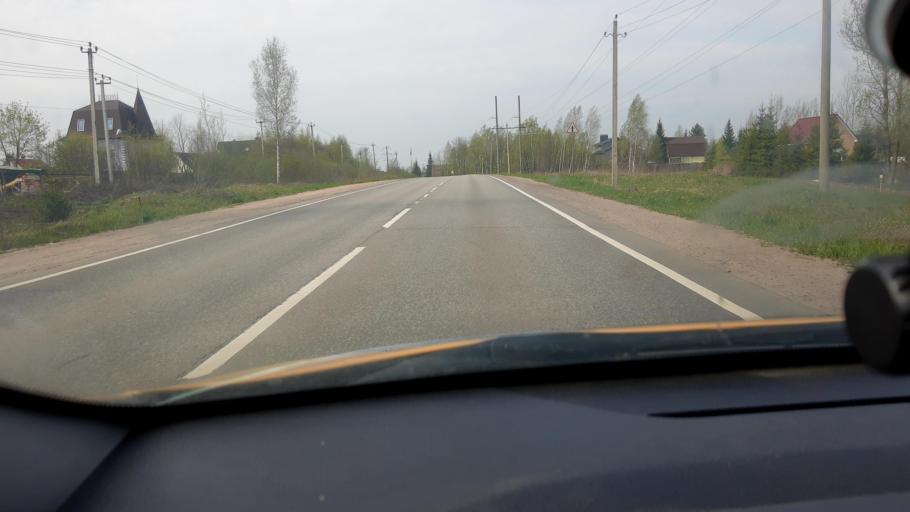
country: RU
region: Moskovskaya
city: Rumyantsevo
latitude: 55.9113
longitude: 36.5920
